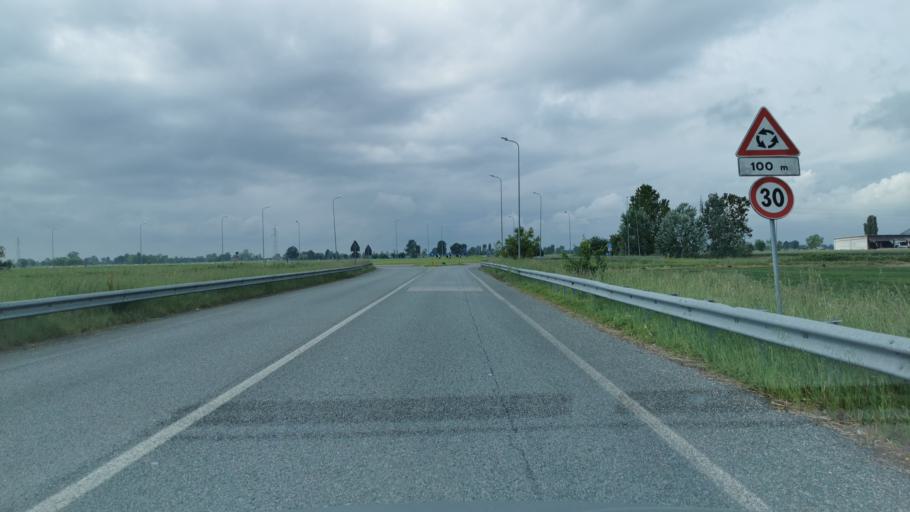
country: IT
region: Piedmont
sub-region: Provincia di Cuneo
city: Racconigi
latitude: 44.7644
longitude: 7.6979
